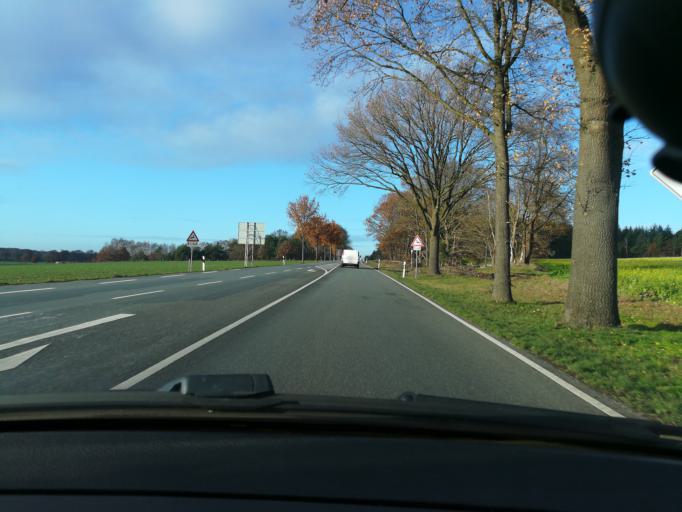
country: DE
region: Lower Saxony
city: Uchte
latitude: 52.5293
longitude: 8.8831
